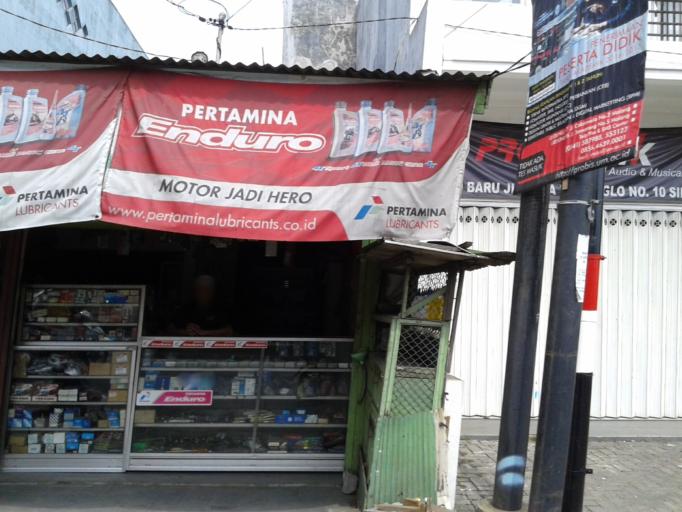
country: ID
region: East Java
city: Singosari
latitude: -7.9149
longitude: 112.6616
